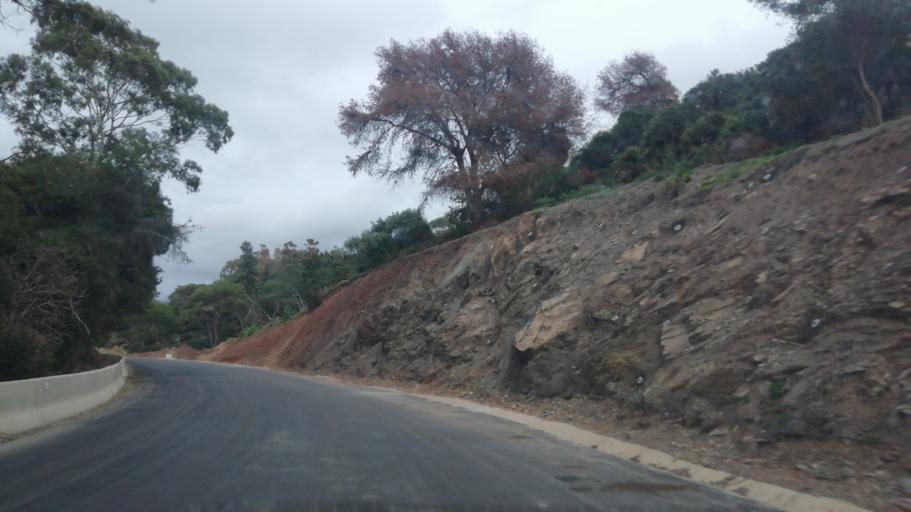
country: DZ
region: Oran
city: Bir el Djir
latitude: 35.7795
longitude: -0.5103
